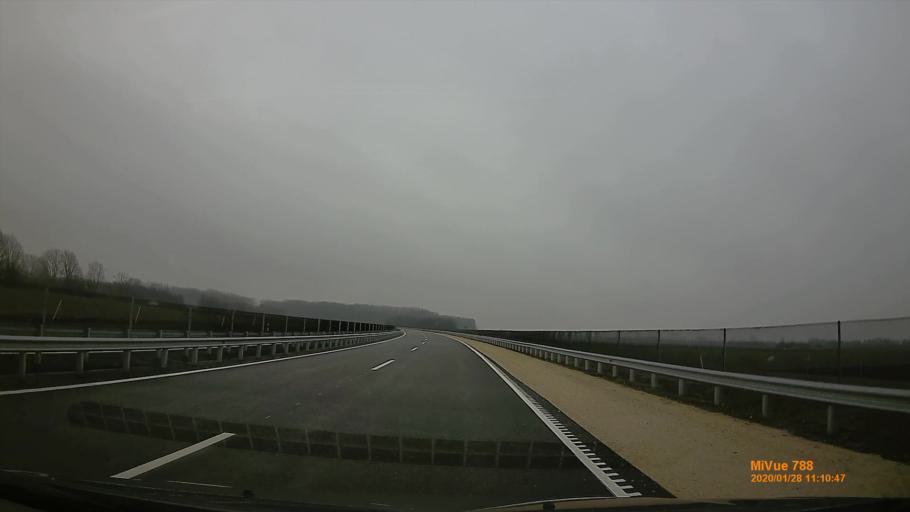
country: HU
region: Pest
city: Ullo
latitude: 47.3846
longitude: 19.3783
